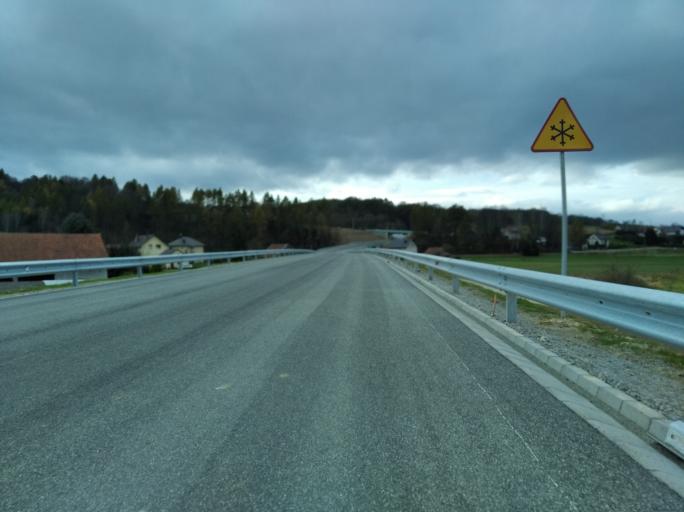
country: PL
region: Subcarpathian Voivodeship
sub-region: Powiat strzyzowski
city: Strzyzow
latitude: 49.8630
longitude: 21.8167
